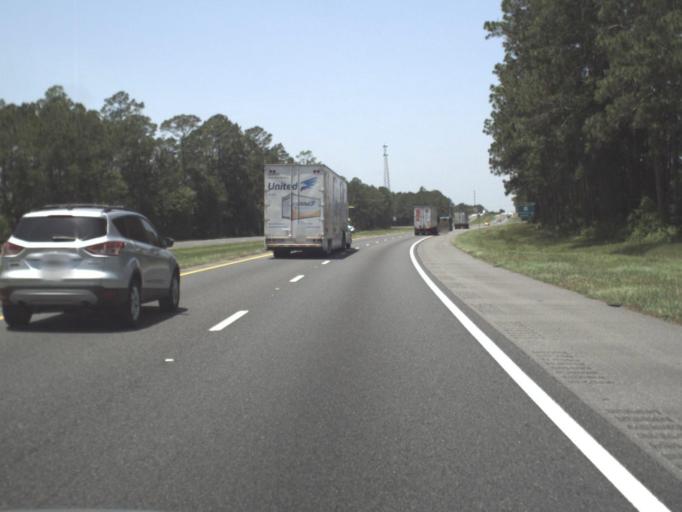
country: US
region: Florida
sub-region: Baker County
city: Macclenny
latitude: 30.2341
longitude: -82.2950
